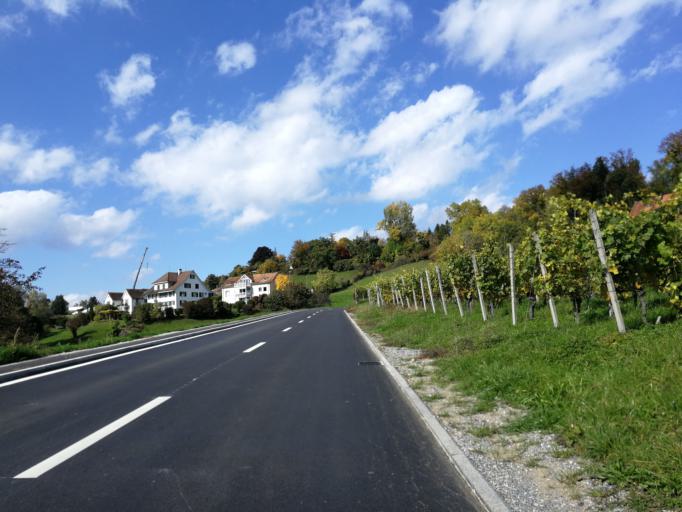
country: CH
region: Zurich
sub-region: Bezirk Meilen
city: Uetikon / Grossdorf
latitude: 47.2701
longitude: 8.6733
